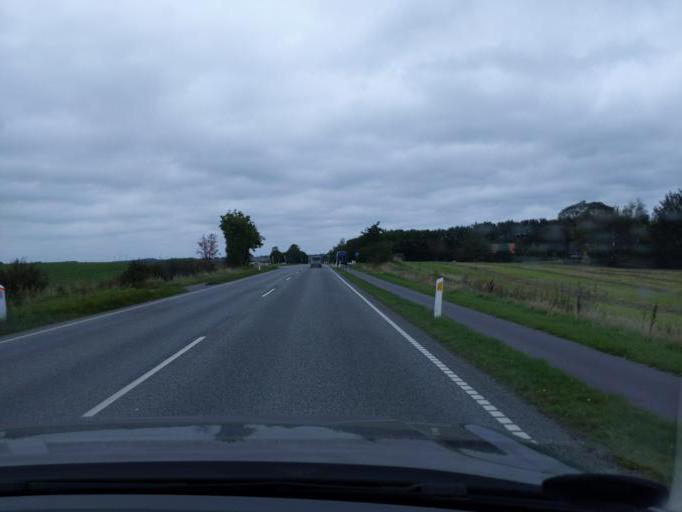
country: DK
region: Central Jutland
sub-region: Randers Kommune
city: Spentrup
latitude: 56.5005
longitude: 9.9638
